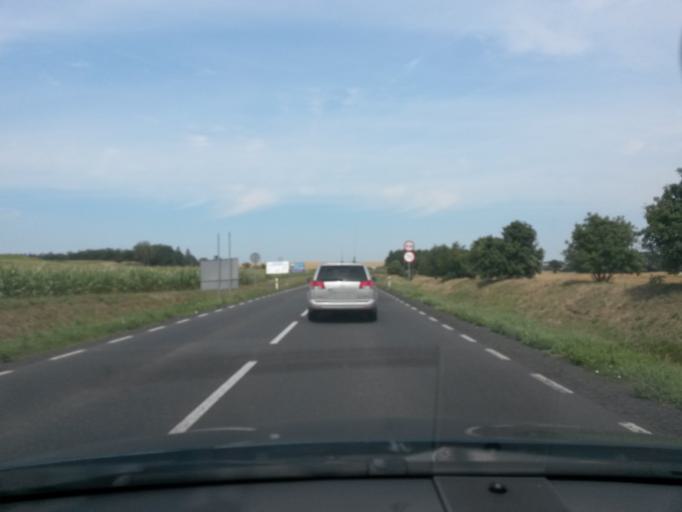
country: PL
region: Greater Poland Voivodeship
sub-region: Powiat gostynski
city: Gostyn
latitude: 51.9147
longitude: 17.0115
